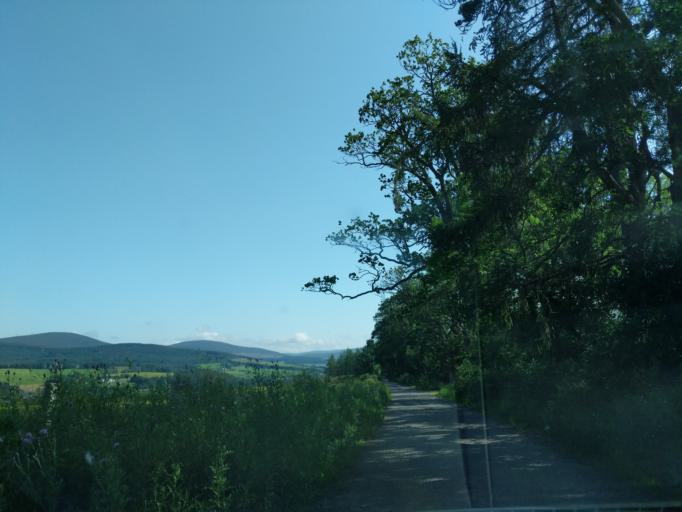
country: GB
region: Scotland
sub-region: Moray
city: Rothes
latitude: 57.4749
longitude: -3.2375
